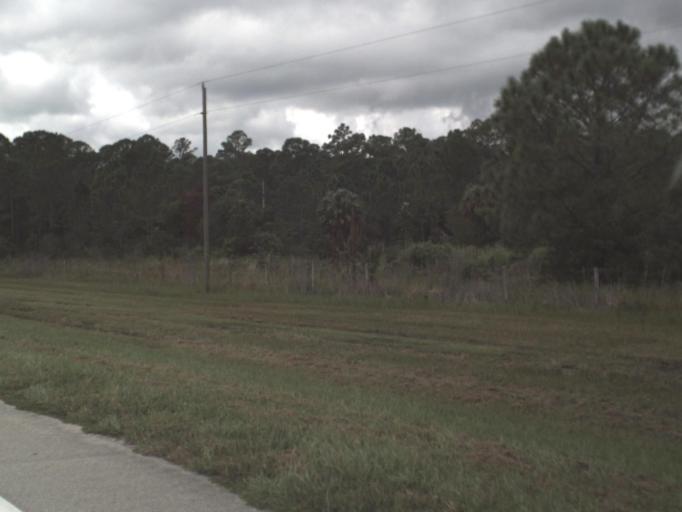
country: US
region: Florida
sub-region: Hendry County
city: Port LaBelle
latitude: 26.8948
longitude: -81.3417
